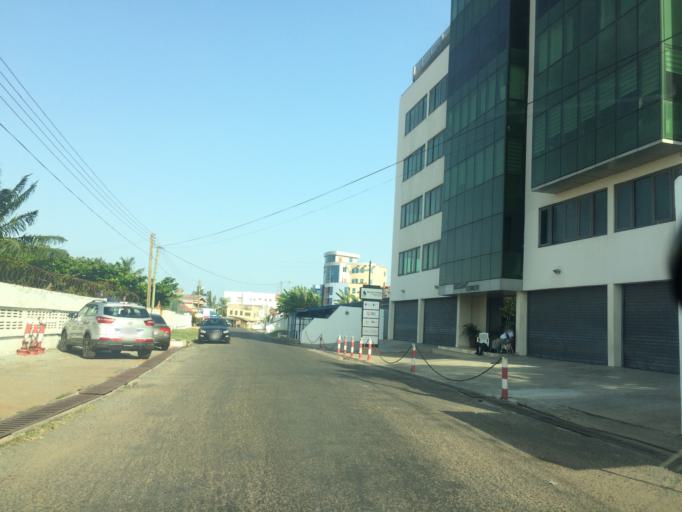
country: GH
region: Greater Accra
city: Accra
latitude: 5.5639
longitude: -0.1859
